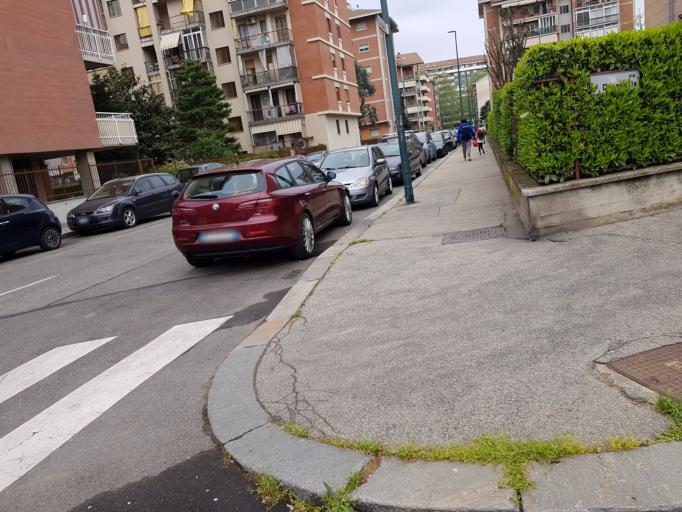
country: IT
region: Piedmont
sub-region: Provincia di Torino
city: Lesna
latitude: 45.0673
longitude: 7.6212
